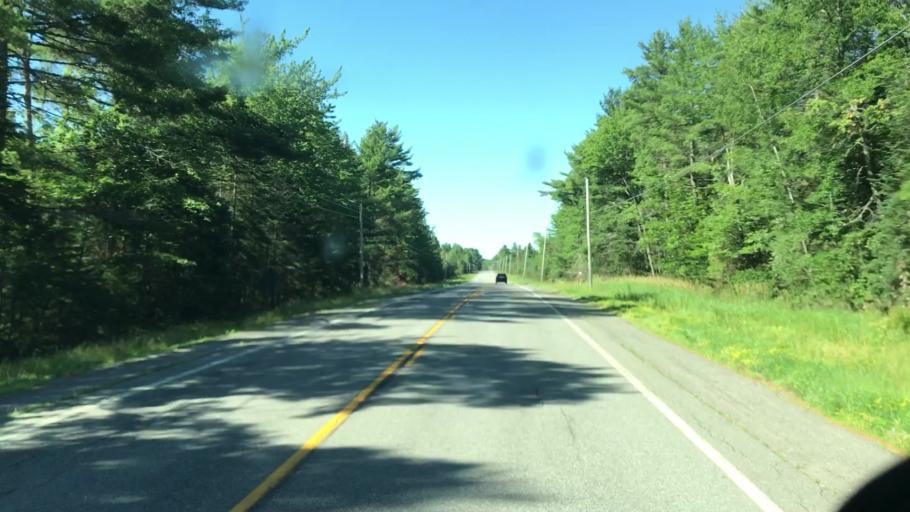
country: US
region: Maine
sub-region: Penobscot County
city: Howland
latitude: 45.2853
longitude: -68.6262
